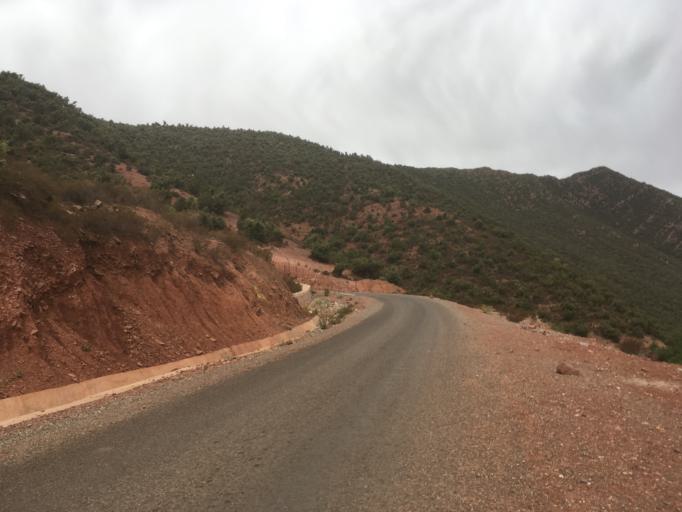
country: MA
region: Marrakech-Tensift-Al Haouz
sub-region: Al-Haouz
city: Tidili Mesfioua
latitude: 31.4019
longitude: -7.5577
